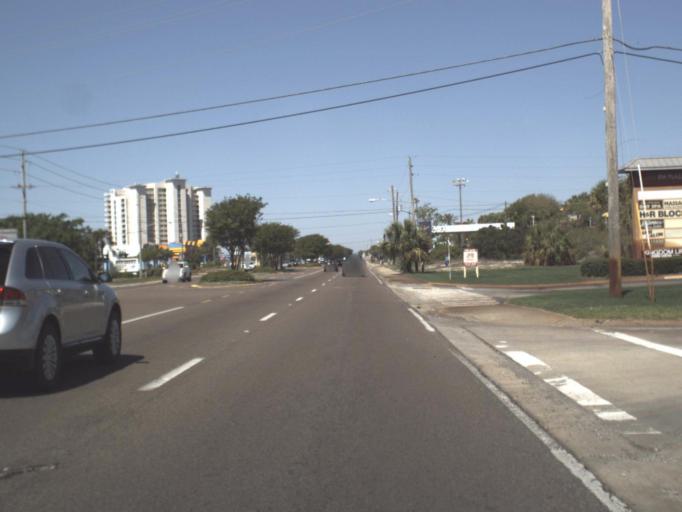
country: US
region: Florida
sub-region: Okaloosa County
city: Destin
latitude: 30.3868
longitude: -86.4699
